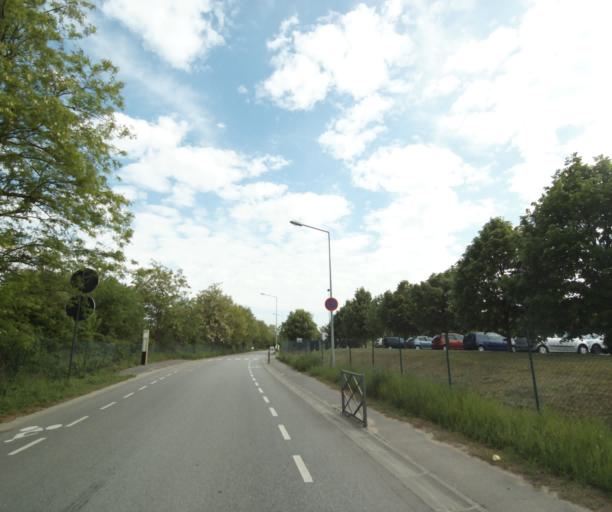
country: FR
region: Ile-de-France
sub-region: Departement des Yvelines
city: Les Mureaux
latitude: 48.9832
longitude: 1.8977
